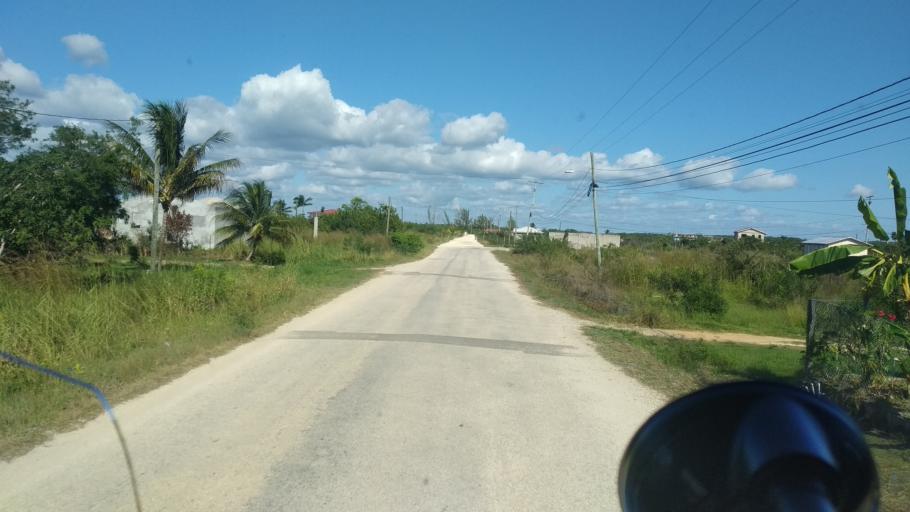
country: BZ
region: Belize
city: Belize City
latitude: 17.5596
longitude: -88.3032
